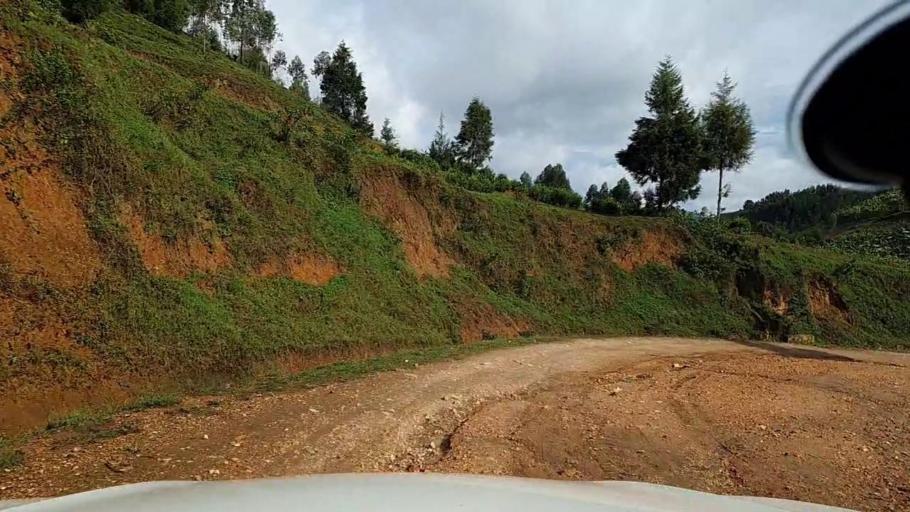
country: RW
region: Western Province
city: Kibuye
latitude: -2.1283
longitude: 29.4986
